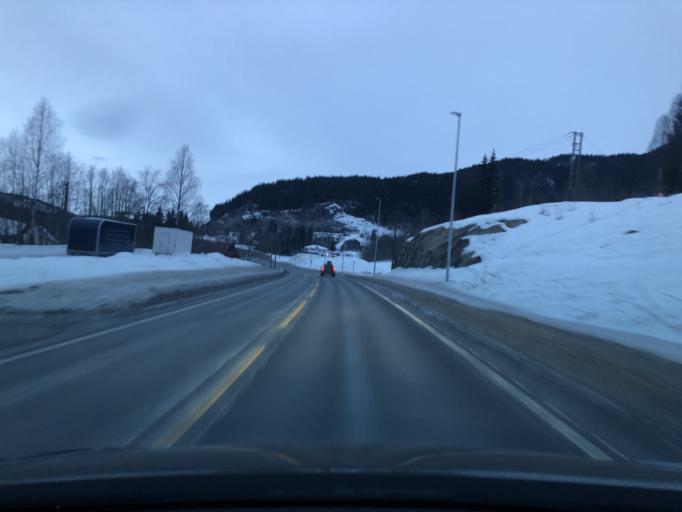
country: NO
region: Oppland
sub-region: Sor-Aurdal
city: Bagn
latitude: 60.8915
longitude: 9.4762
